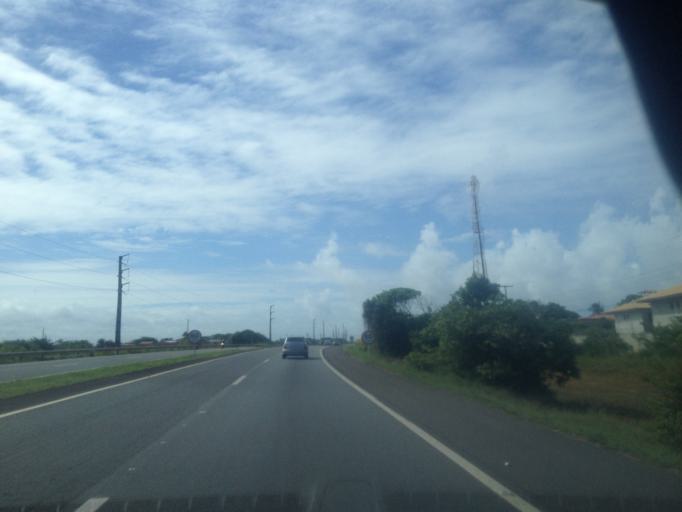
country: BR
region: Bahia
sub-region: Camacari
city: Camacari
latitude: -12.6509
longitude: -38.0833
